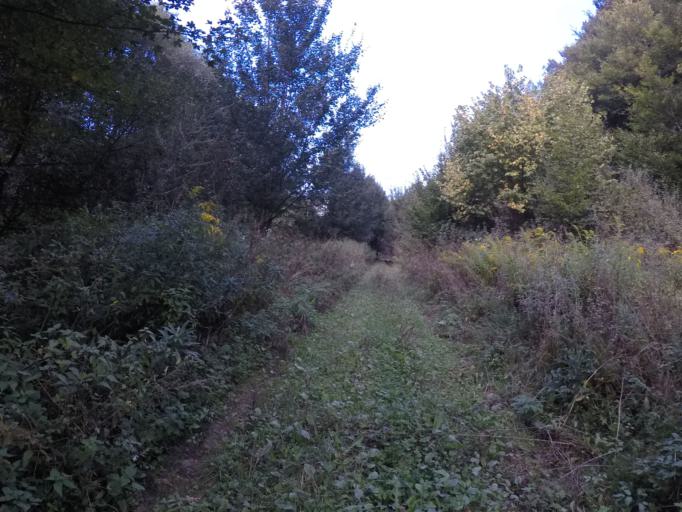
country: SK
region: Presovsky
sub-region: Okres Presov
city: Presov
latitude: 48.9318
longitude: 21.1658
